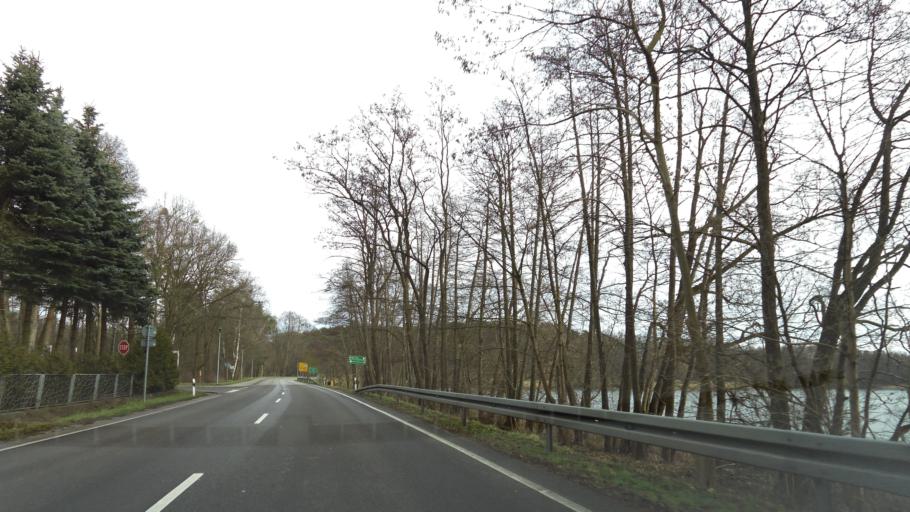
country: DE
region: Brandenburg
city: Strausberg
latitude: 52.5926
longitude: 13.8884
